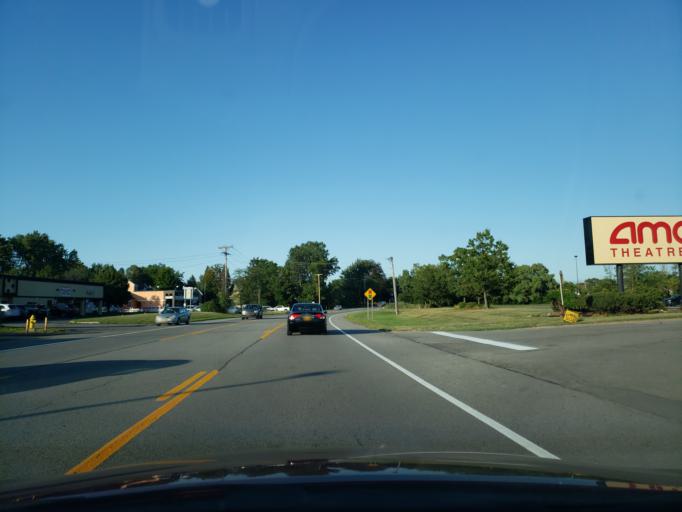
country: US
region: New York
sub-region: Monroe County
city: Webster
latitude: 43.2025
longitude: -77.4956
